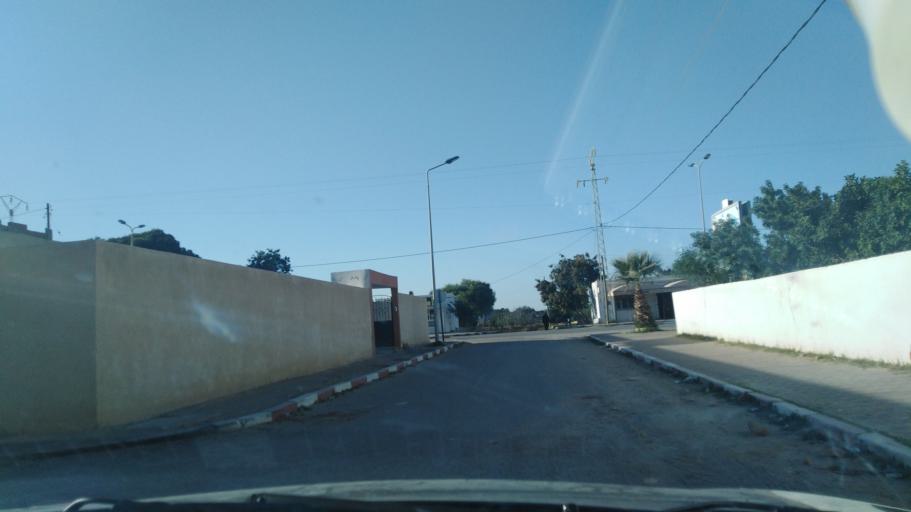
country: TN
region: Al Mahdiyah
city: Shurban
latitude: 34.9655
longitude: 10.3679
